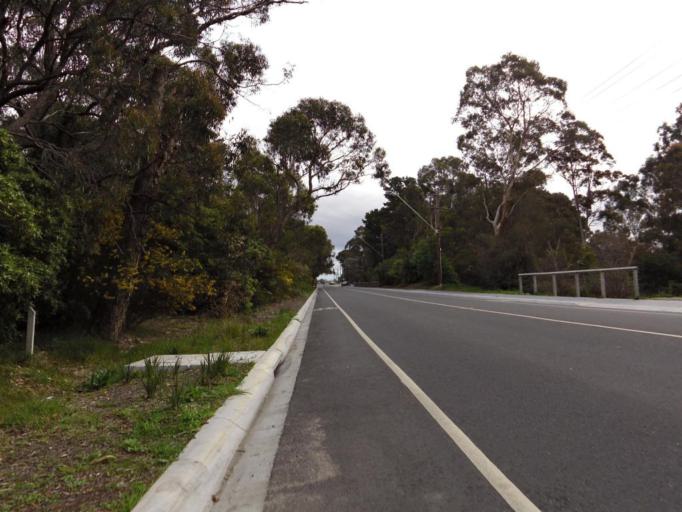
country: AU
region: Victoria
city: Mitcham
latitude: -37.7959
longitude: 145.1966
